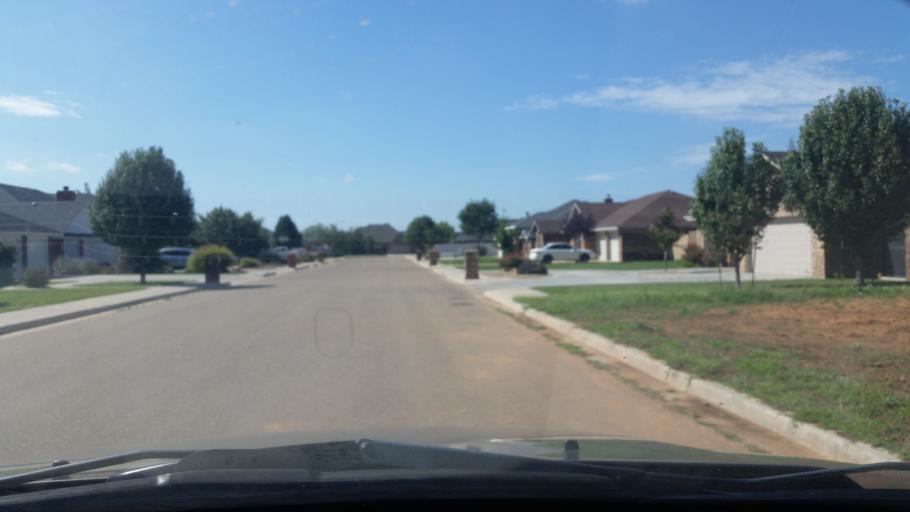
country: US
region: New Mexico
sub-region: Curry County
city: Clovis
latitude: 34.4377
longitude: -103.1767
